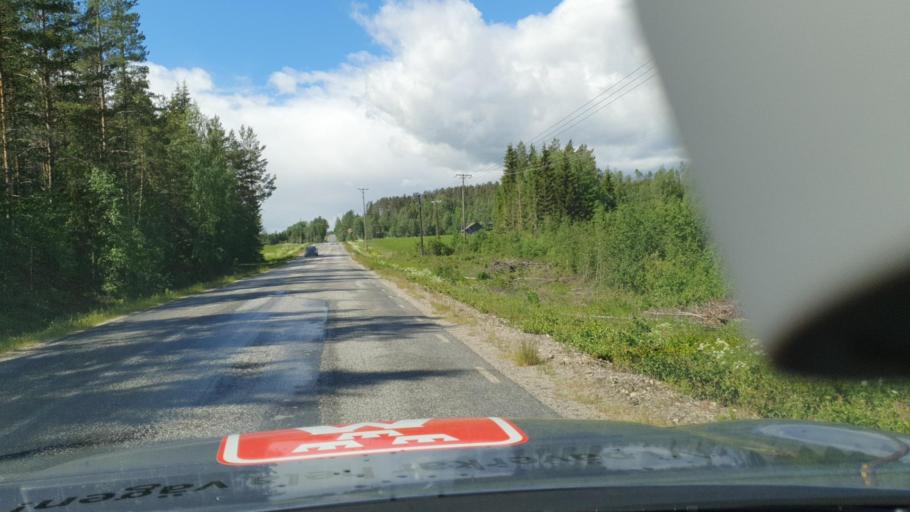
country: SE
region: Vaesternorrland
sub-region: OErnskoeldsviks Kommun
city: Bredbyn
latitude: 63.3726
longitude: 17.9500
